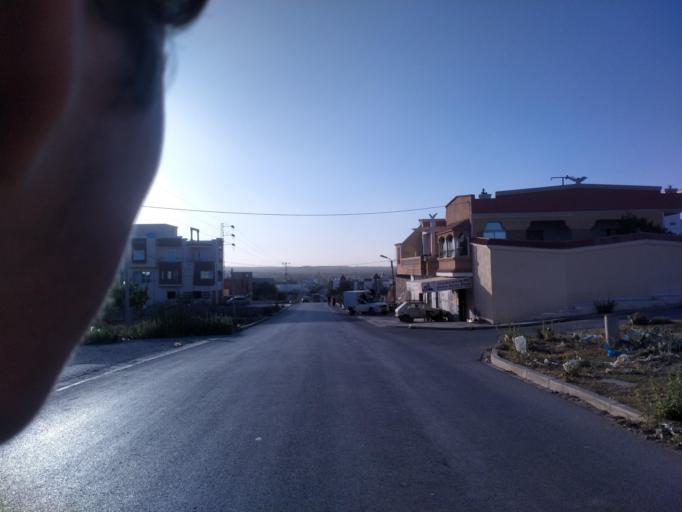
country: TN
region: Susah
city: Akouda
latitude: 35.8162
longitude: 10.5553
